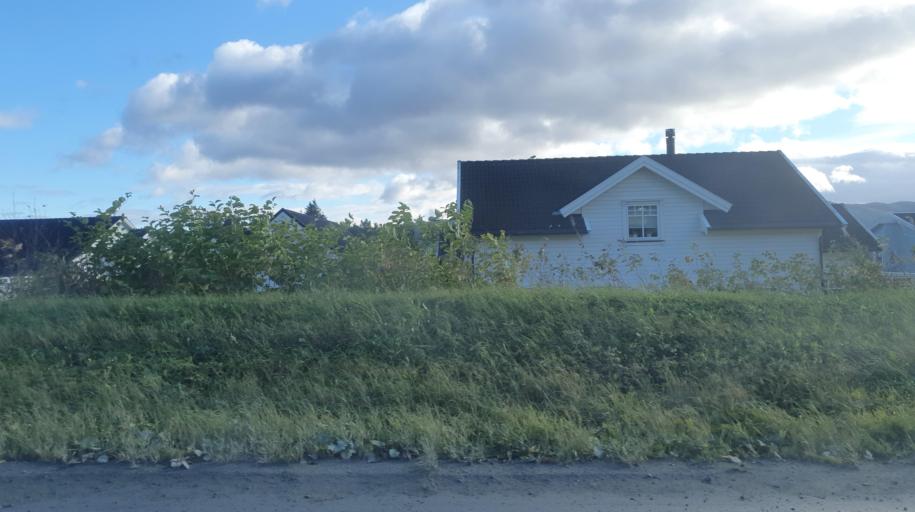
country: NO
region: Sor-Trondelag
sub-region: Klaebu
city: Klaebu
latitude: 63.3111
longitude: 10.4304
